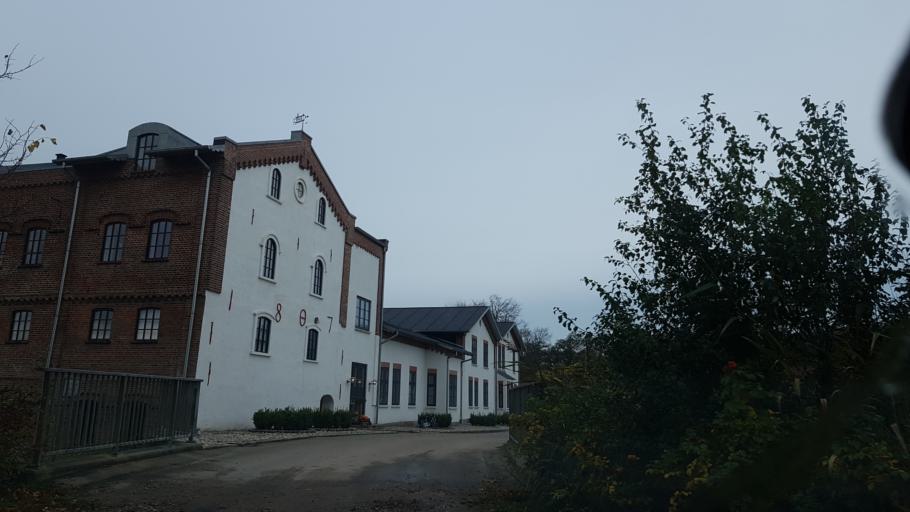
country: DK
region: South Denmark
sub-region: Tonder Kommune
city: Sherrebek
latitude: 55.1940
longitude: 8.7544
